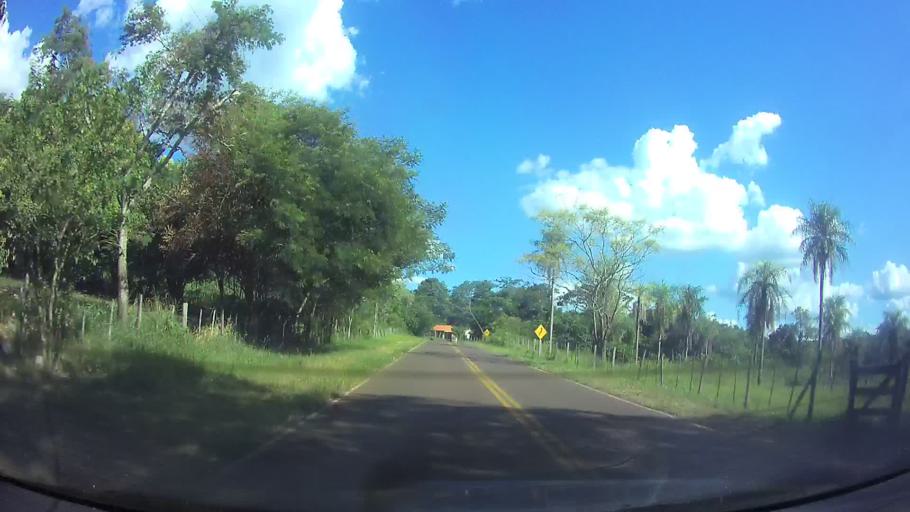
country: PY
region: Paraguari
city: Sapucai
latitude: -25.6475
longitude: -56.8638
